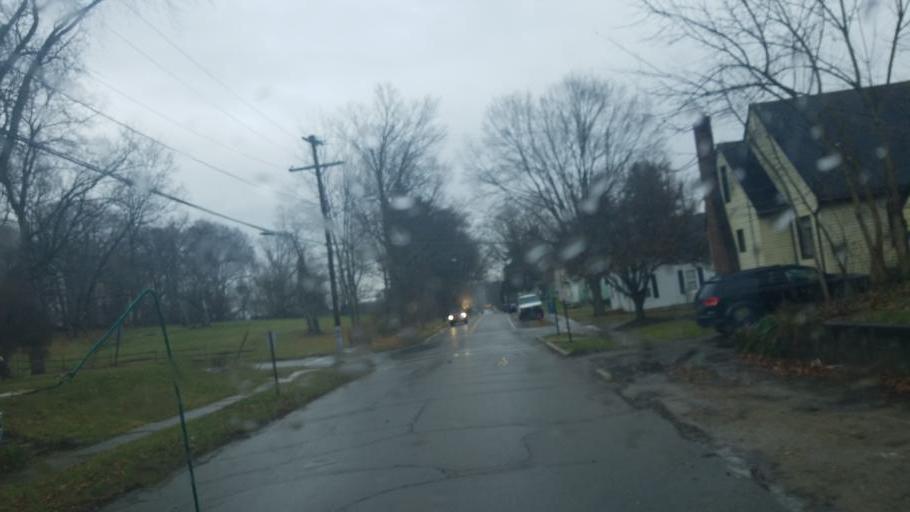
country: US
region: Ohio
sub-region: Knox County
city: Mount Vernon
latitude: 40.3981
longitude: -82.4816
